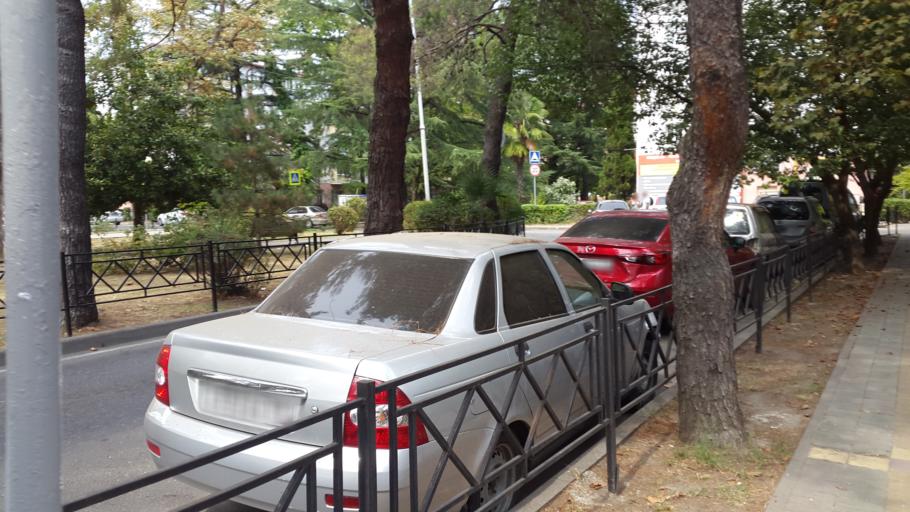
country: RU
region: Krasnodarskiy
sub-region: Sochi City
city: Sochi
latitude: 43.6018
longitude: 39.7259
